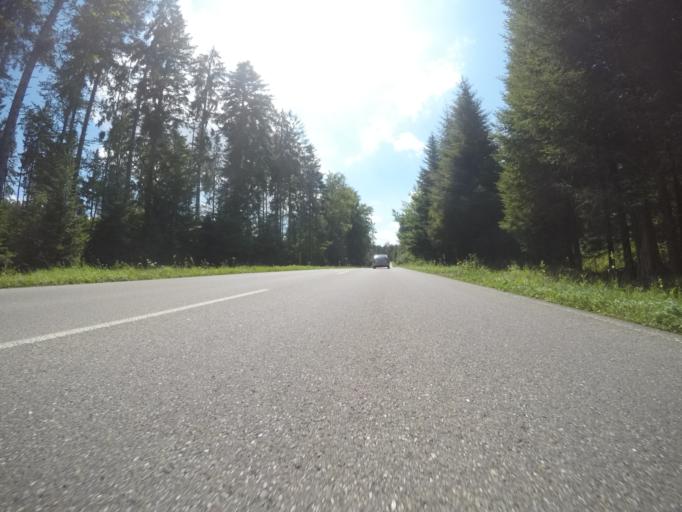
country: DE
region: Baden-Wuerttemberg
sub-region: Karlsruhe Region
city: Wornersberg
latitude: 48.5472
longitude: 8.5753
